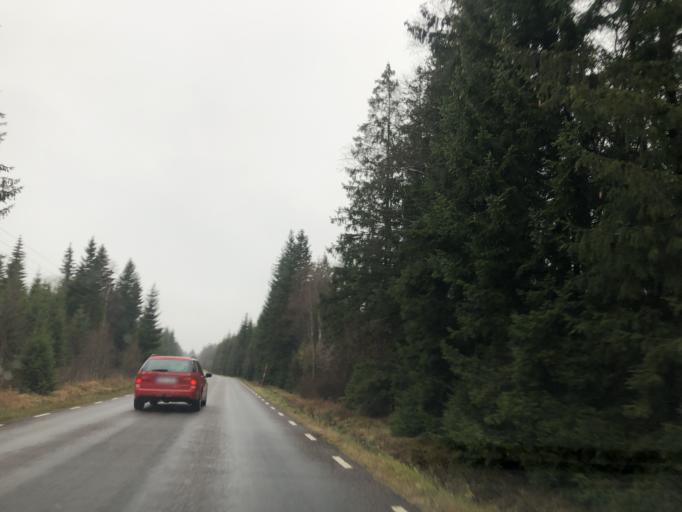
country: SE
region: Vaestra Goetaland
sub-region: Ulricehamns Kommun
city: Ulricehamn
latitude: 57.7471
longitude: 13.5291
